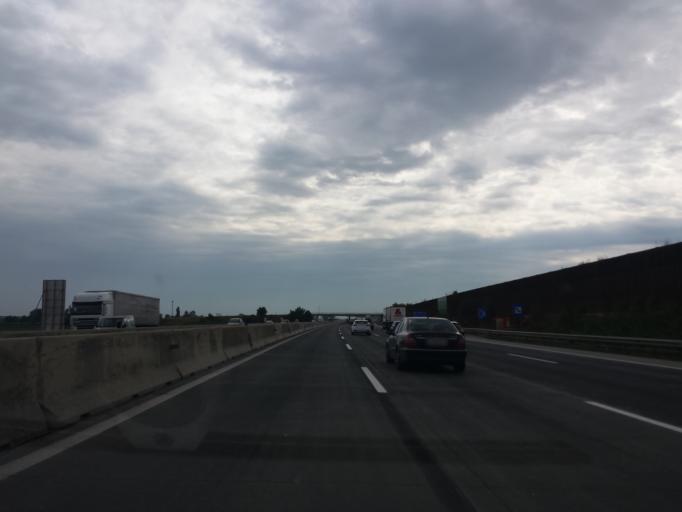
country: AT
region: Lower Austria
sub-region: Politischer Bezirk Modling
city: Guntramsdorf
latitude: 48.0221
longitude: 16.3310
